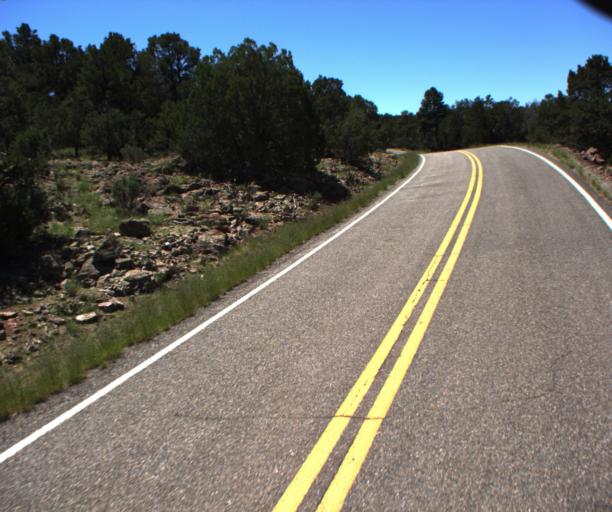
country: US
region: Arizona
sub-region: Greenlee County
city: Morenci
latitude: 33.3753
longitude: -109.3297
